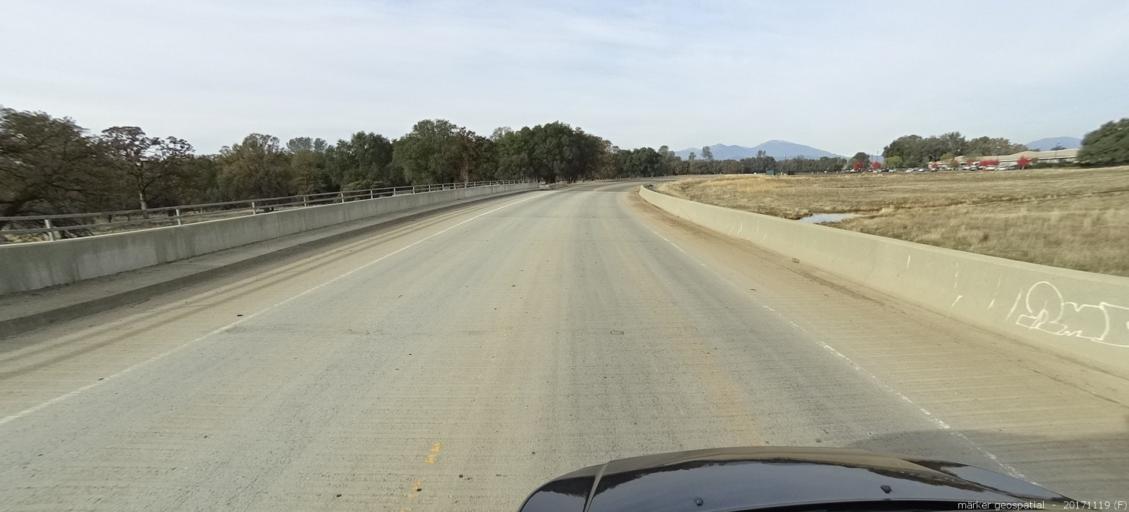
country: US
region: California
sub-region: Shasta County
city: Anderson
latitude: 40.5056
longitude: -122.3078
